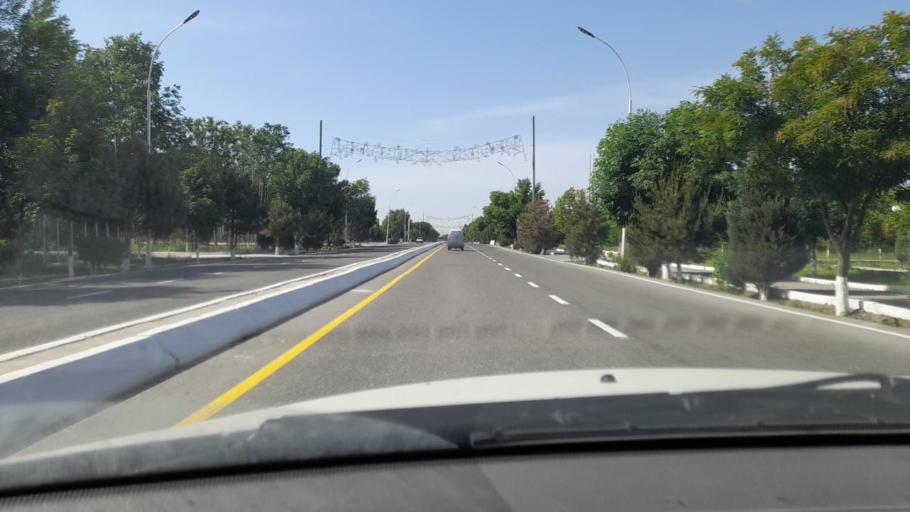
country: UZ
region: Bukhara
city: Bukhara
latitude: 39.7956
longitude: 64.4347
